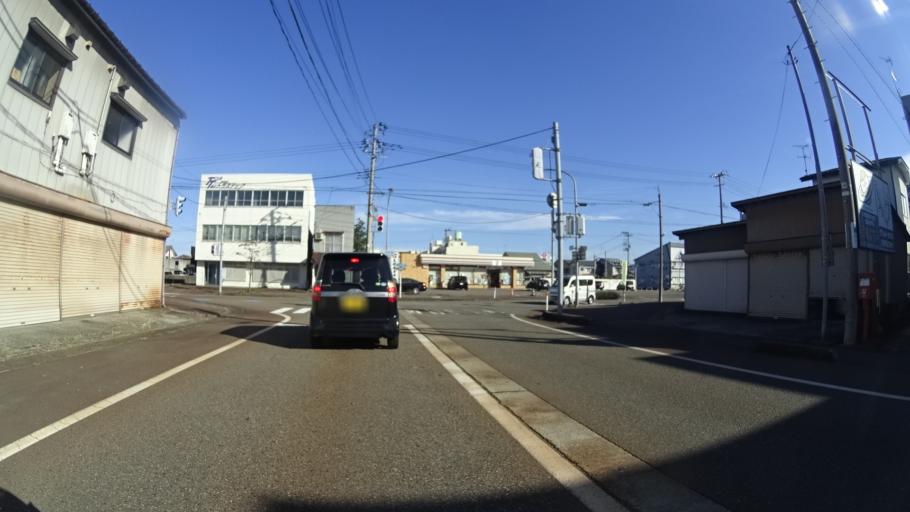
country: JP
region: Niigata
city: Mitsuke
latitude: 37.5386
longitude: 138.9079
